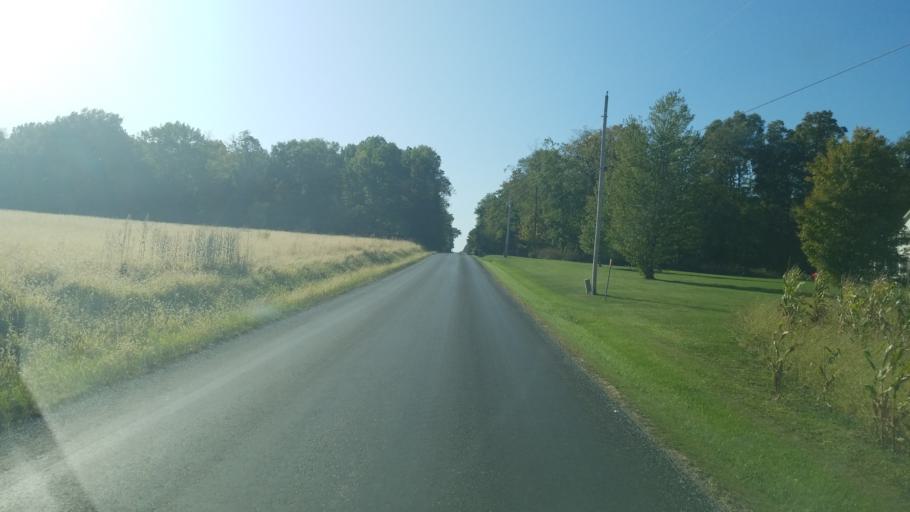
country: US
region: Ohio
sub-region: Wayne County
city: Creston
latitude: 40.9302
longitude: -81.9808
